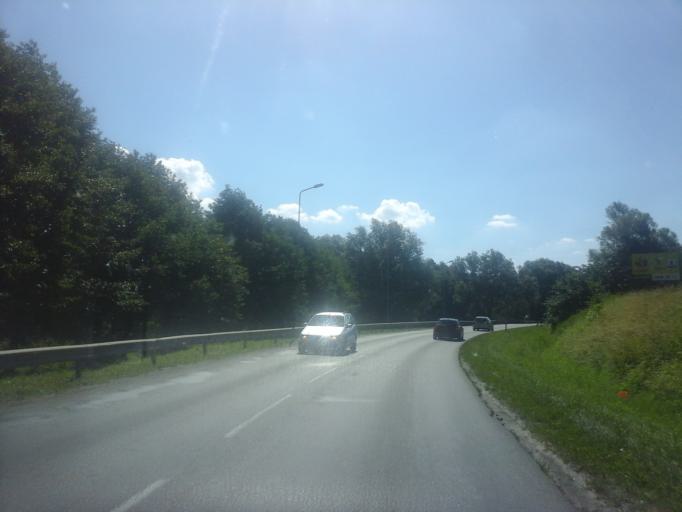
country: PL
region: West Pomeranian Voivodeship
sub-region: Powiat bialogardzki
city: Bialogard
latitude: 54.0031
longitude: 15.9857
